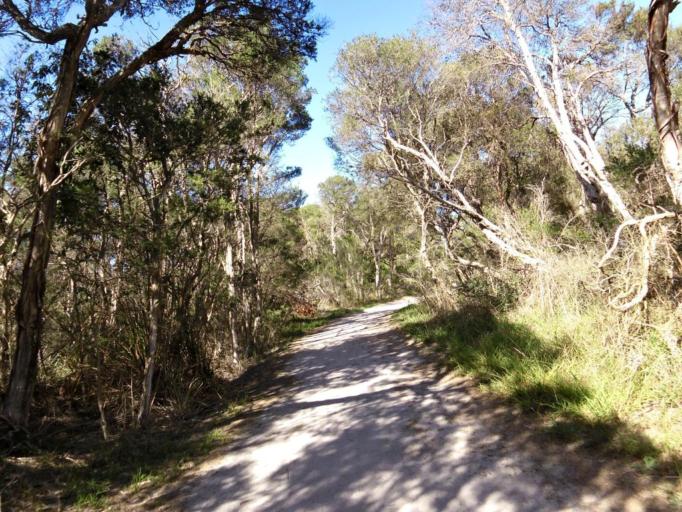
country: AU
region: Victoria
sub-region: Bass Coast
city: North Wonthaggi
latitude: -38.6080
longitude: 145.6029
